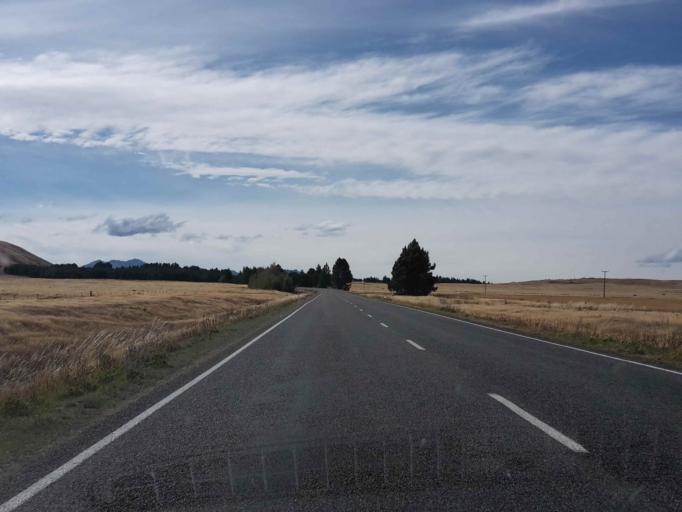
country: NZ
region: Canterbury
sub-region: Timaru District
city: Pleasant Point
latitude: -44.0229
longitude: 170.4017
